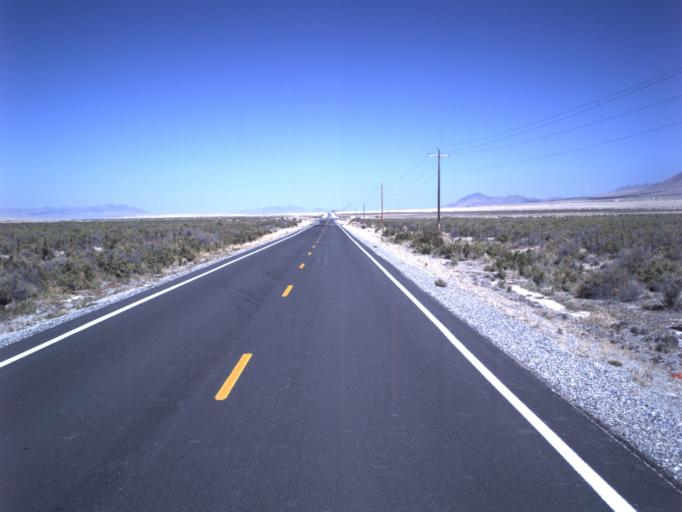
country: US
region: Utah
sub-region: Tooele County
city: Grantsville
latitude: 40.3488
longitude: -112.7452
